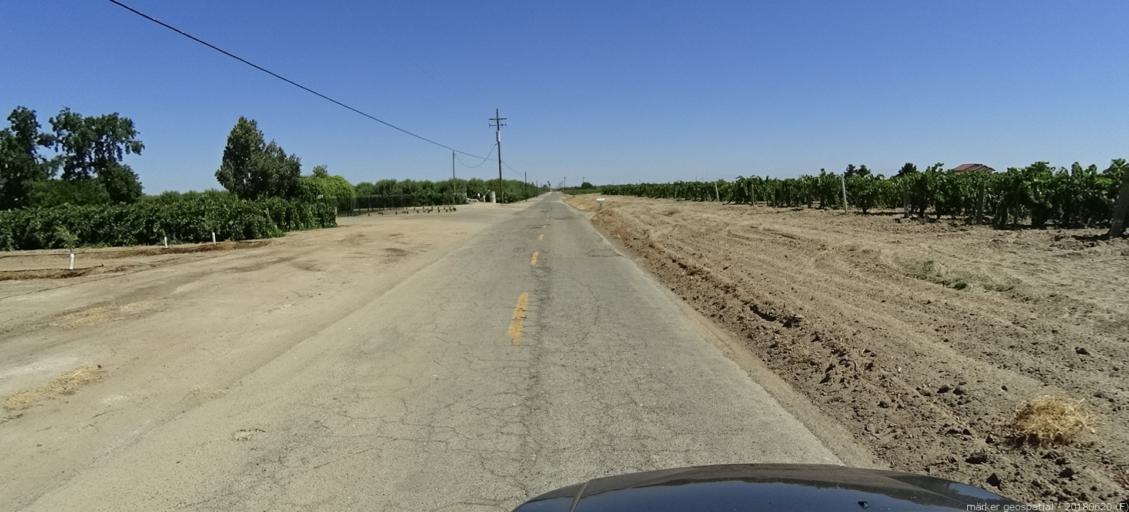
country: US
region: California
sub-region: Madera County
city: Parkwood
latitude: 36.8986
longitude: -120.0105
